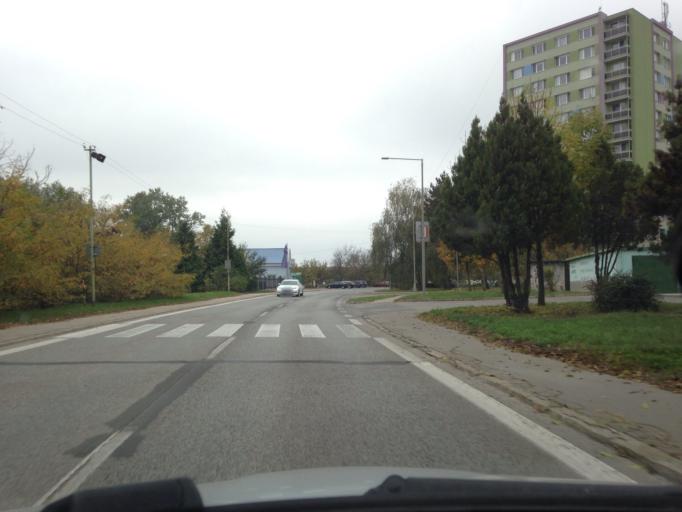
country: SK
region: Nitriansky
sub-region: Okres Nove Zamky
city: Sturovo
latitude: 47.7909
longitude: 18.7222
